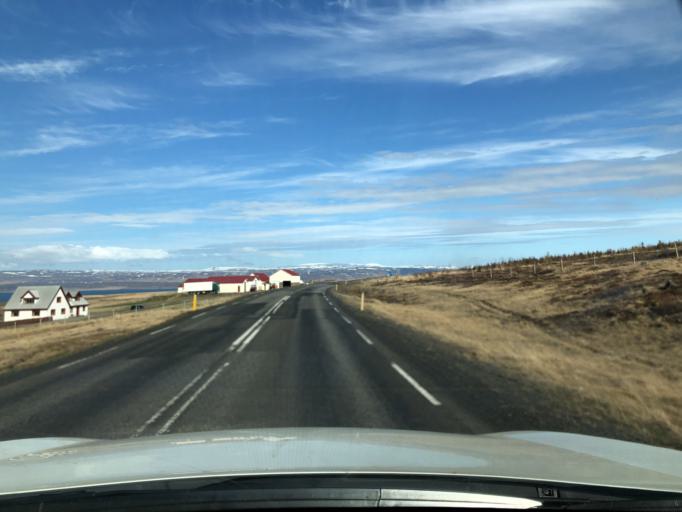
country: IS
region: West
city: Borgarnes
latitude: 65.0681
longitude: -21.7716
